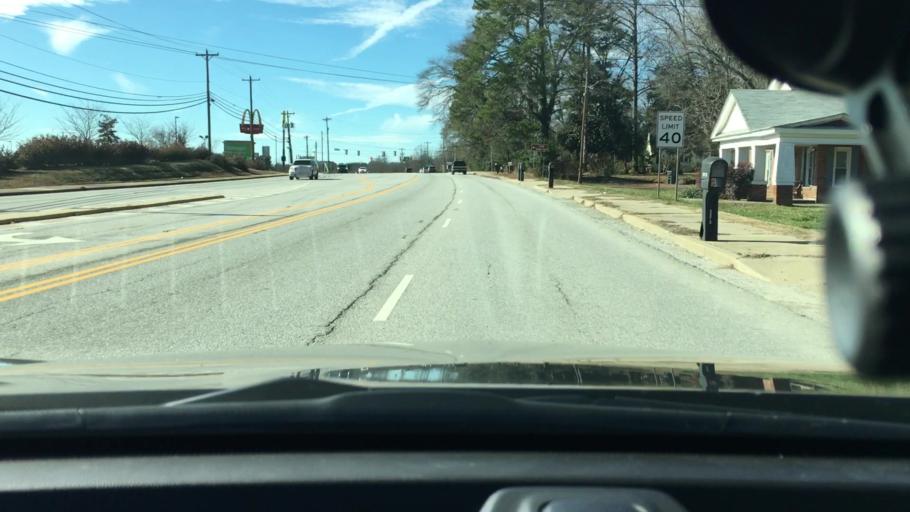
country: US
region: South Carolina
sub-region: Spartanburg County
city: Spartanburg
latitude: 34.9220
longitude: -81.8844
